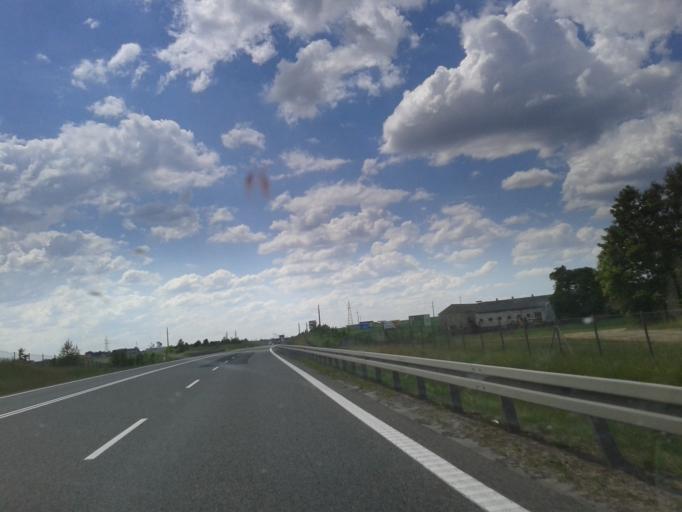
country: PL
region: Pomeranian Voivodeship
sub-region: Powiat chojnicki
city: Chojnice
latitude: 53.6995
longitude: 17.6312
